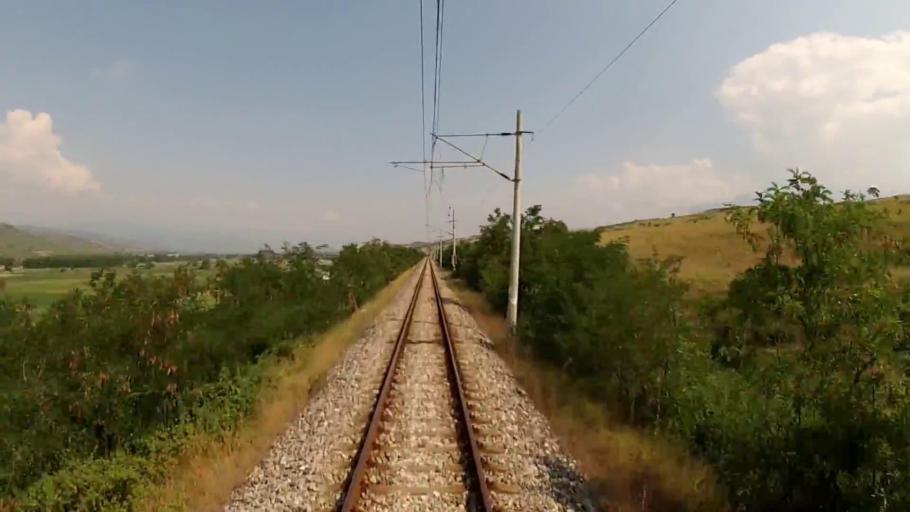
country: BG
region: Blagoevgrad
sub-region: Obshtina Sandanski
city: Sandanski
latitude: 41.5834
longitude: 23.2386
